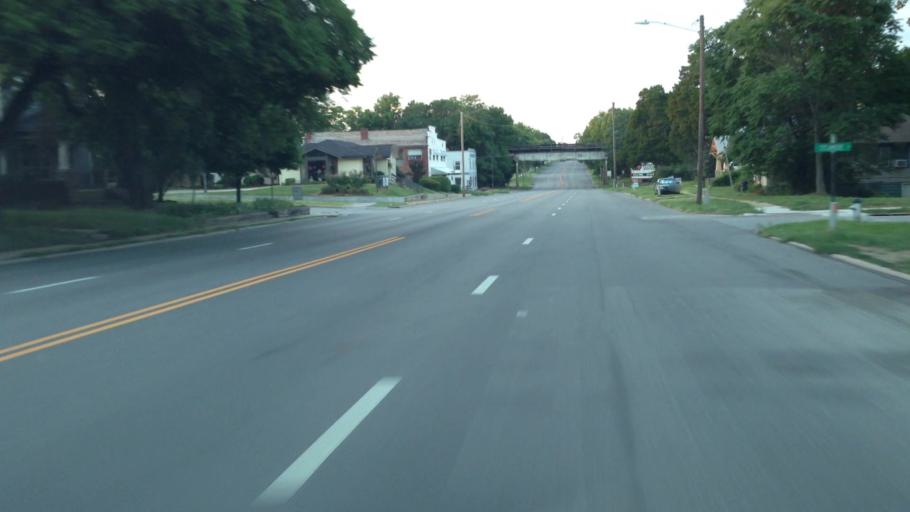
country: US
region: Kansas
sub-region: Montgomery County
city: Independence
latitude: 37.2306
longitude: -95.7065
